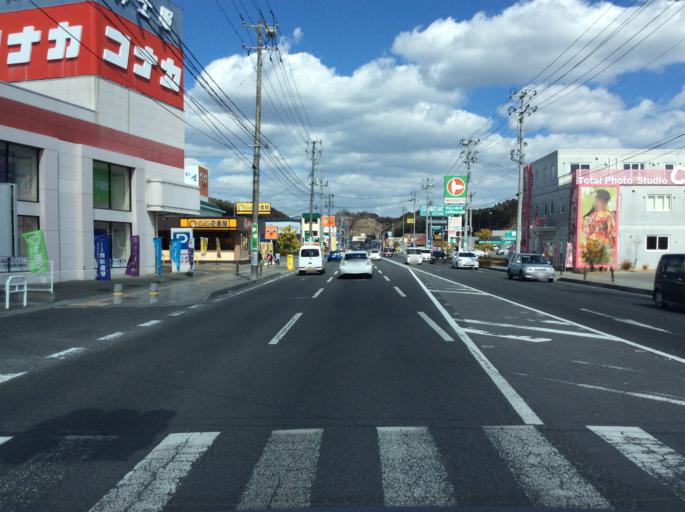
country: JP
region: Fukushima
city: Iwaki
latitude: 36.9620
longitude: 140.9042
